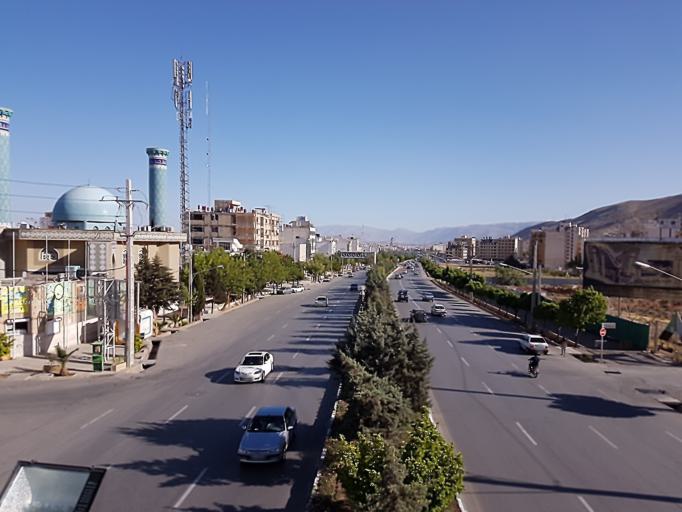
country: IR
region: Fars
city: Shiraz
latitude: 29.6703
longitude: 52.4552
